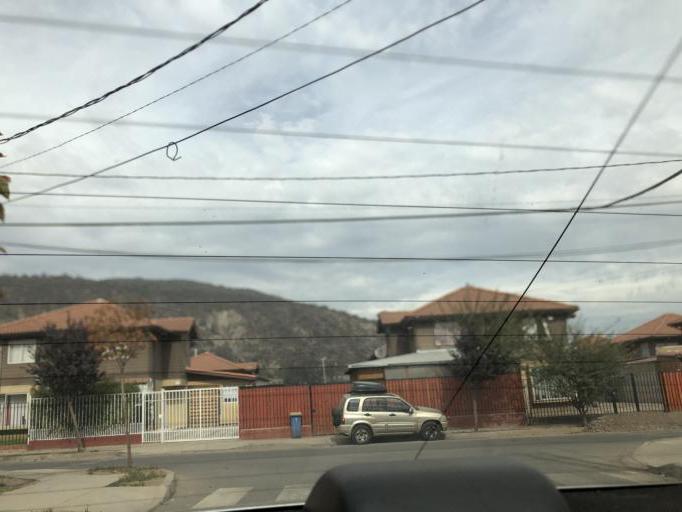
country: CL
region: Santiago Metropolitan
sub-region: Provincia de Cordillera
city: Puente Alto
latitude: -33.6133
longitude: -70.5274
